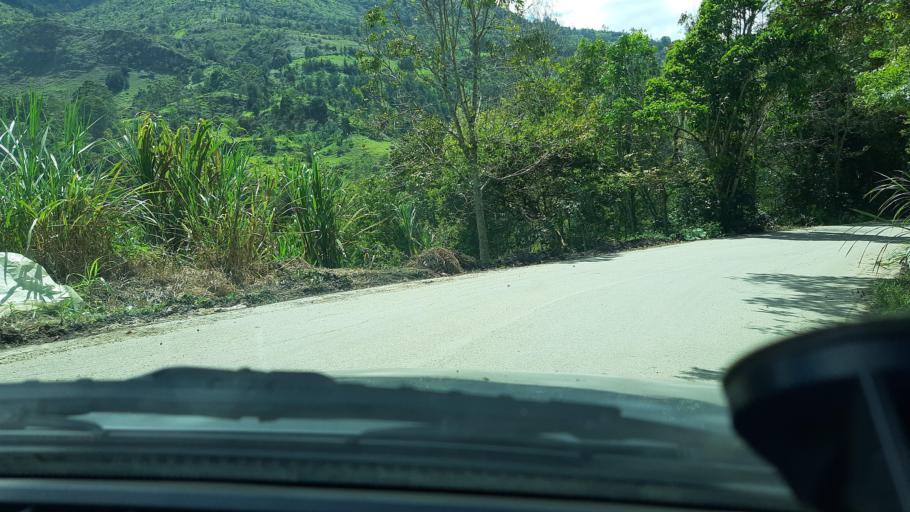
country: CO
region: Boyaca
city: Chinavita
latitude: 5.1780
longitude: -73.3827
